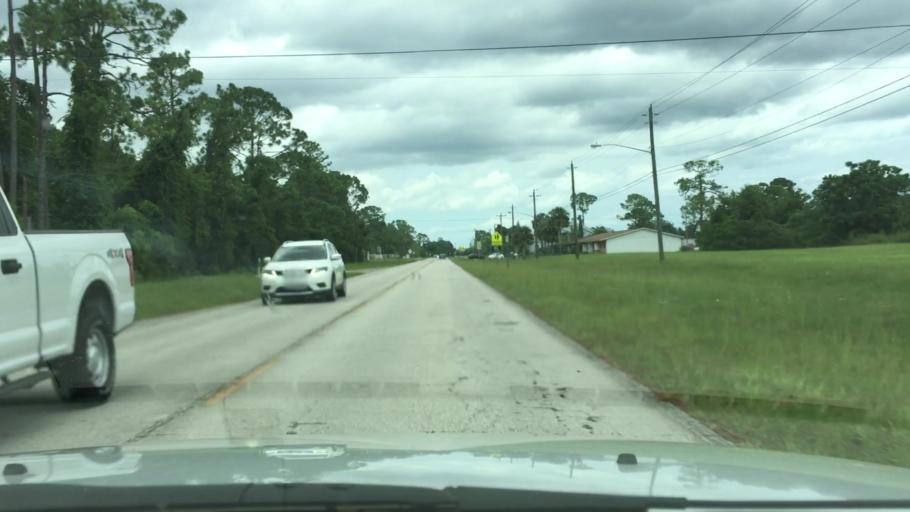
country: US
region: Florida
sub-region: Volusia County
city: Holly Hill
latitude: 29.2211
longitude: -81.0703
